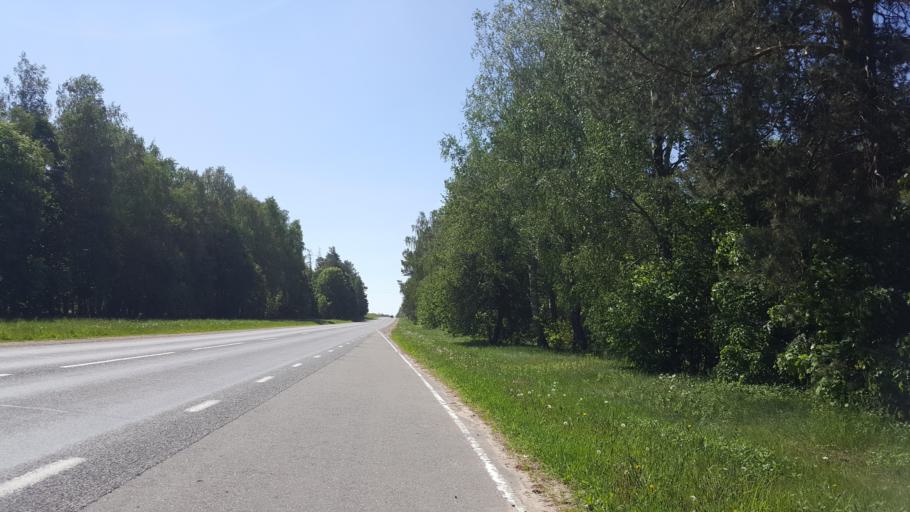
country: BY
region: Brest
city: Kamyanyets
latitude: 52.3529
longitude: 23.7765
